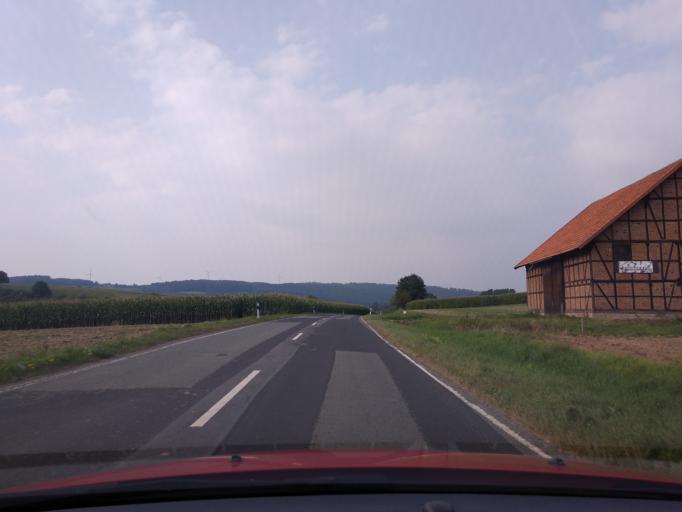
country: DE
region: Hesse
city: Liebenau
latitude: 51.4879
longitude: 9.2976
